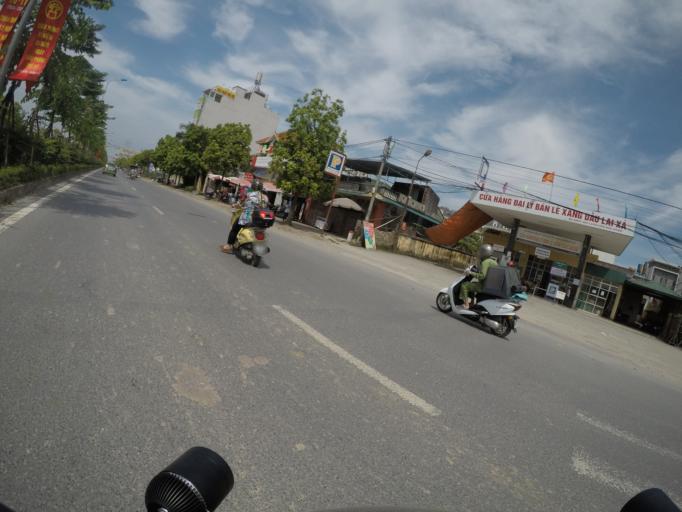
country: VN
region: Ha Noi
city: Troi
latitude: 21.0663
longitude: 105.7144
